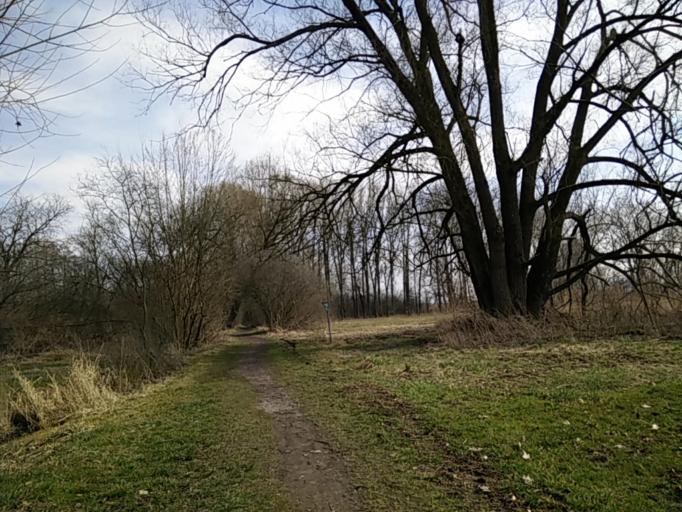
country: DE
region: Baden-Wuerttemberg
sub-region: Freiburg Region
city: Radolfzell am Bodensee
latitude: 47.7383
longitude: 9.0038
